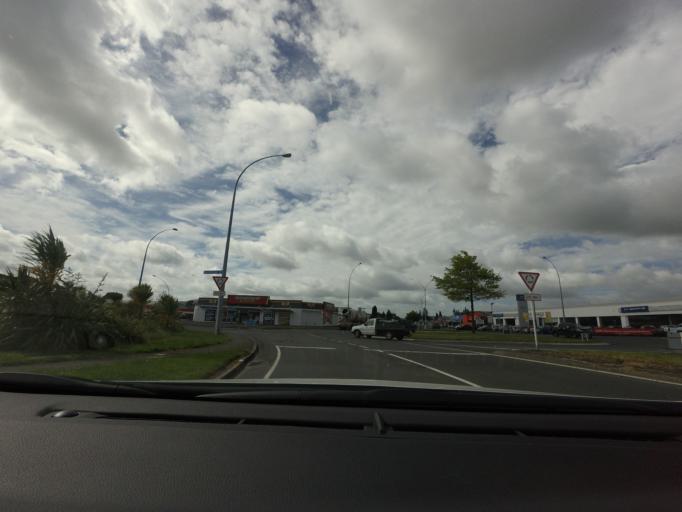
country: NZ
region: Bay of Plenty
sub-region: Rotorua District
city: Rotorua
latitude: -38.1293
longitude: 176.2330
